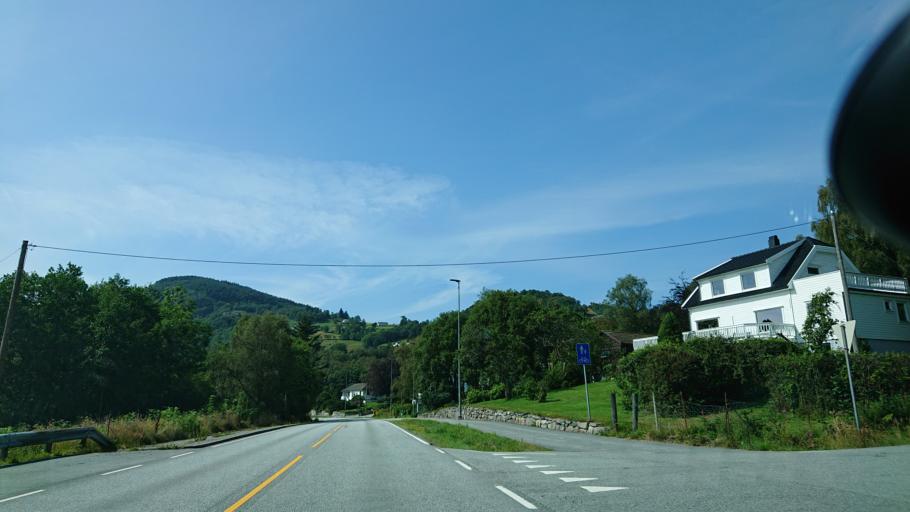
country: NO
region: Rogaland
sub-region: Strand
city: Jorpeland
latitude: 59.0706
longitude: 6.0029
